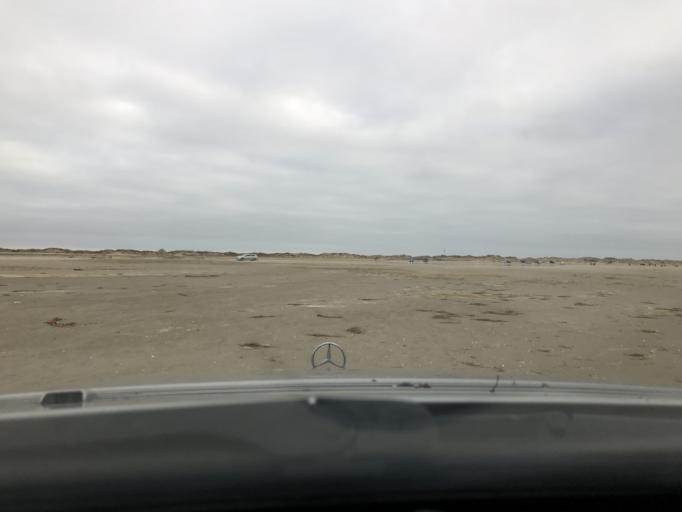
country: DE
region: Schleswig-Holstein
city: List
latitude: 55.1512
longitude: 8.4813
